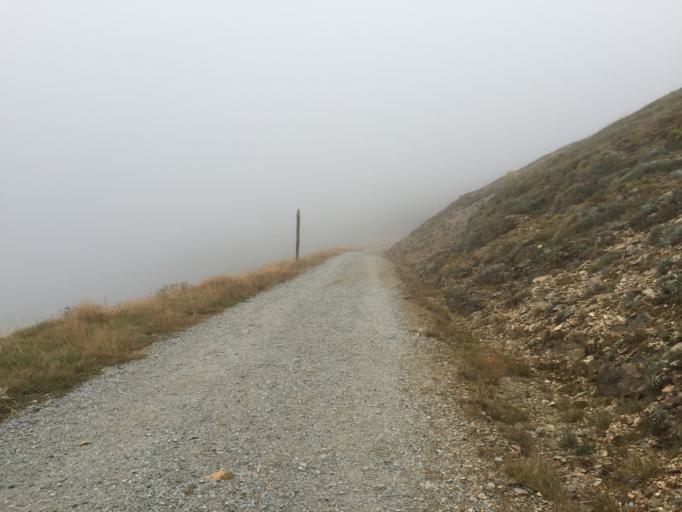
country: AU
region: New South Wales
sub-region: Snowy River
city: Jindabyne
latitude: -36.4557
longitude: 148.2717
